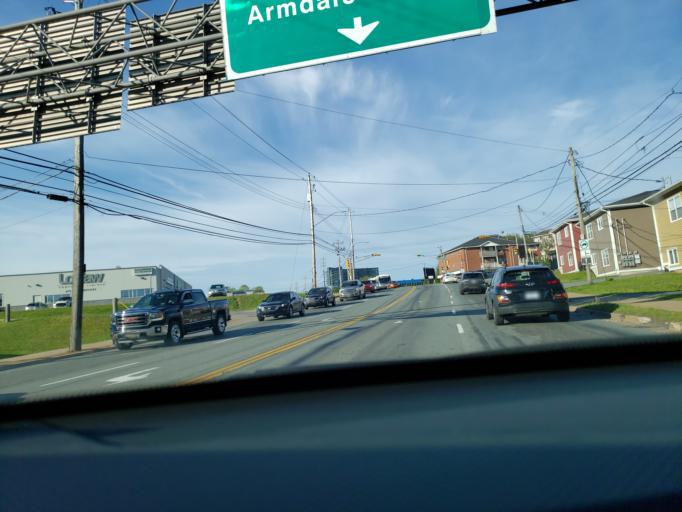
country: CA
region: Nova Scotia
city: Dartmouth
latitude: 44.6607
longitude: -63.6281
